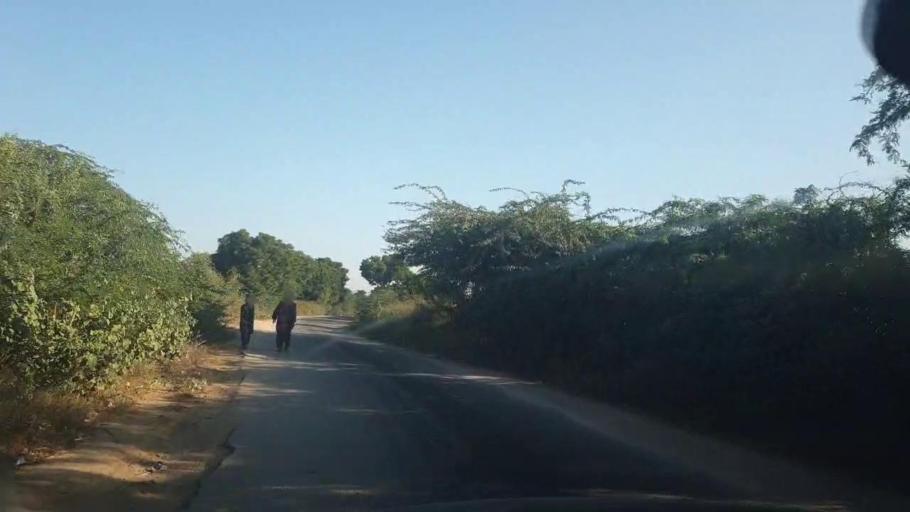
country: PK
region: Sindh
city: Malir Cantonment
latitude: 25.1040
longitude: 67.2587
